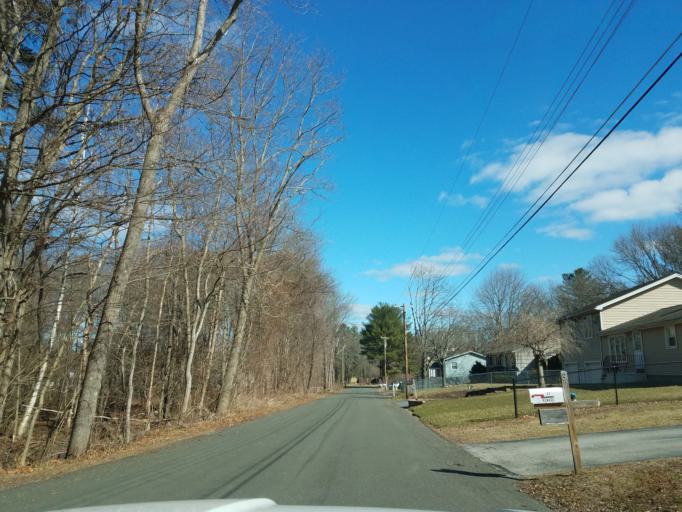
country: US
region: Massachusetts
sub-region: Worcester County
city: Webster
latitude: 42.0238
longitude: -71.8735
